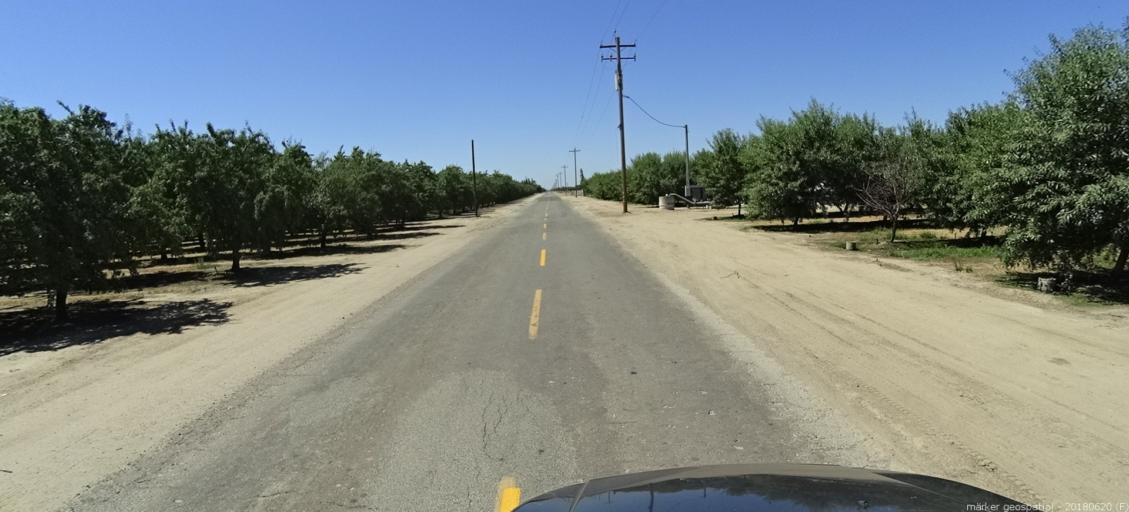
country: US
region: California
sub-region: Madera County
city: Parkwood
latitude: 36.8945
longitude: -120.0015
